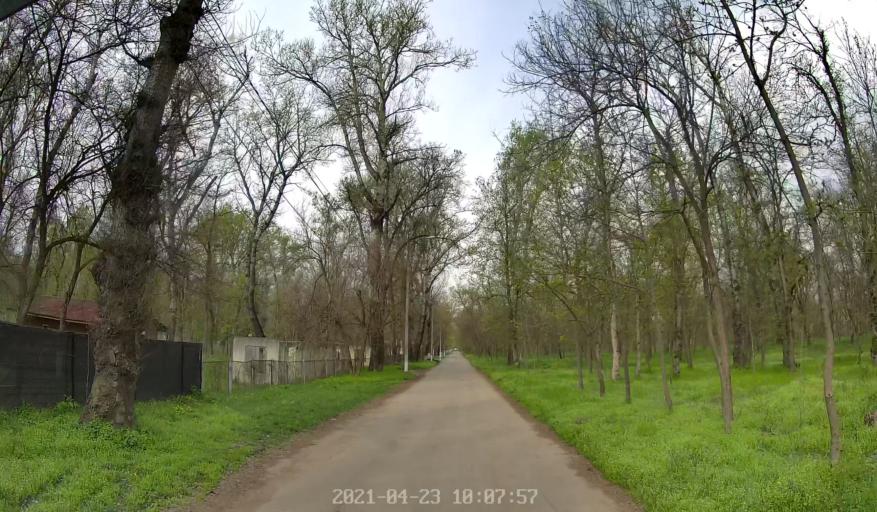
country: MD
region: Chisinau
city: Vadul lui Voda
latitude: 47.0862
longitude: 29.1083
